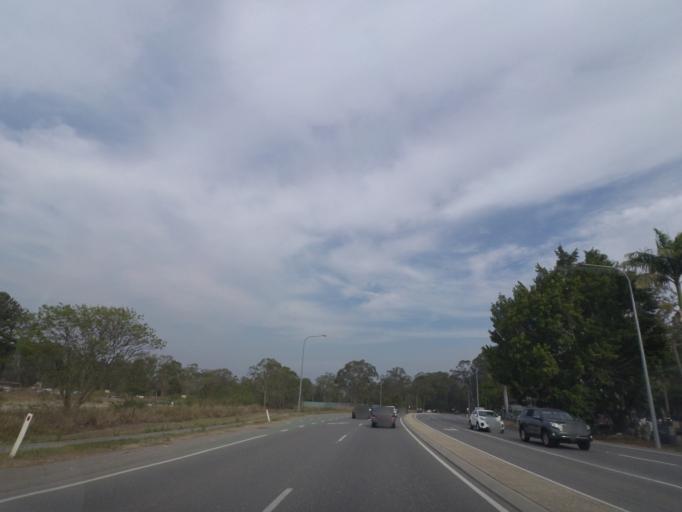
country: AU
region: Queensland
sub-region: Brisbane
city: Inala
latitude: -27.5944
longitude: 153.0053
